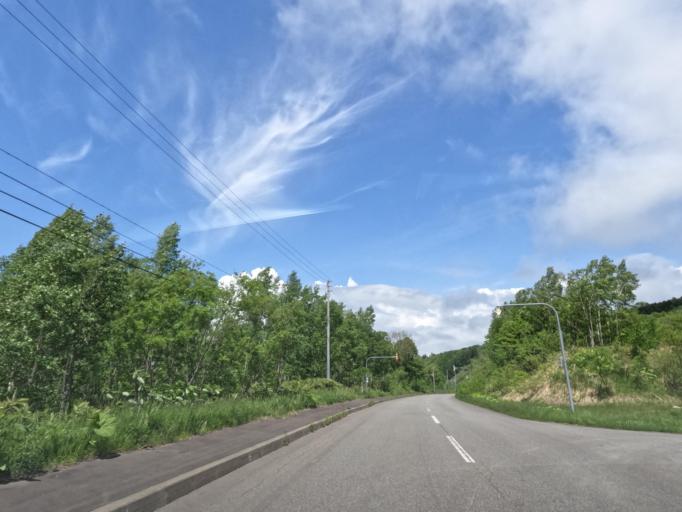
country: JP
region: Hokkaido
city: Tobetsu
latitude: 43.3705
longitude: 141.5742
